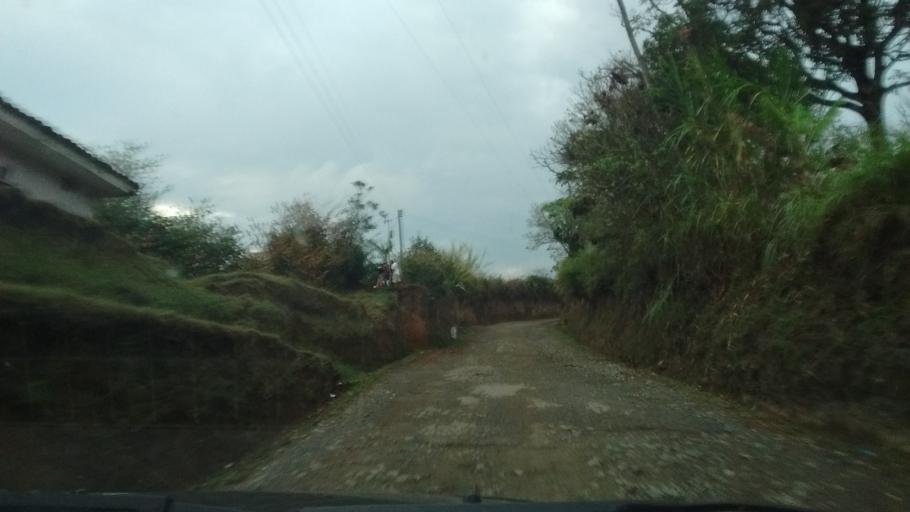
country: CO
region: Cauca
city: Lopez
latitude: 2.3814
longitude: -76.7205
